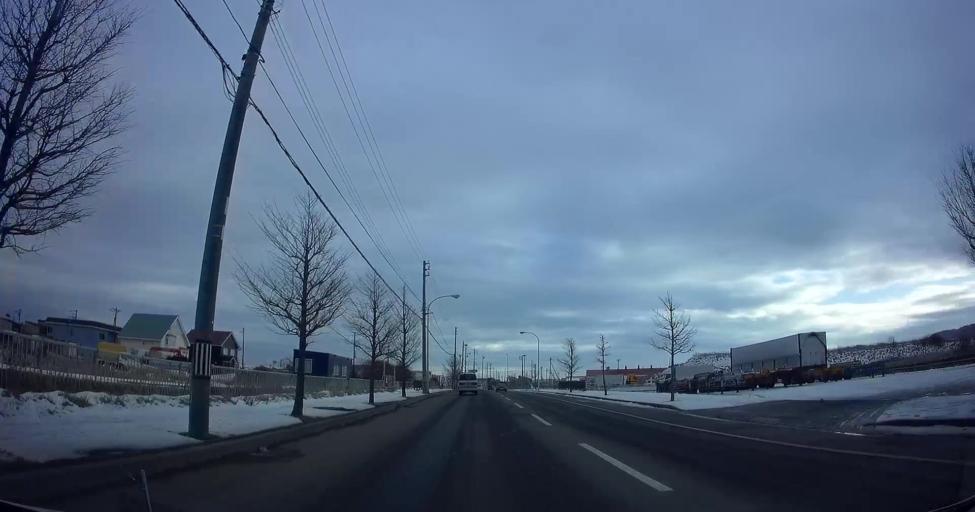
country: JP
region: Hokkaido
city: Hakodate
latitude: 41.8073
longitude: 140.7157
